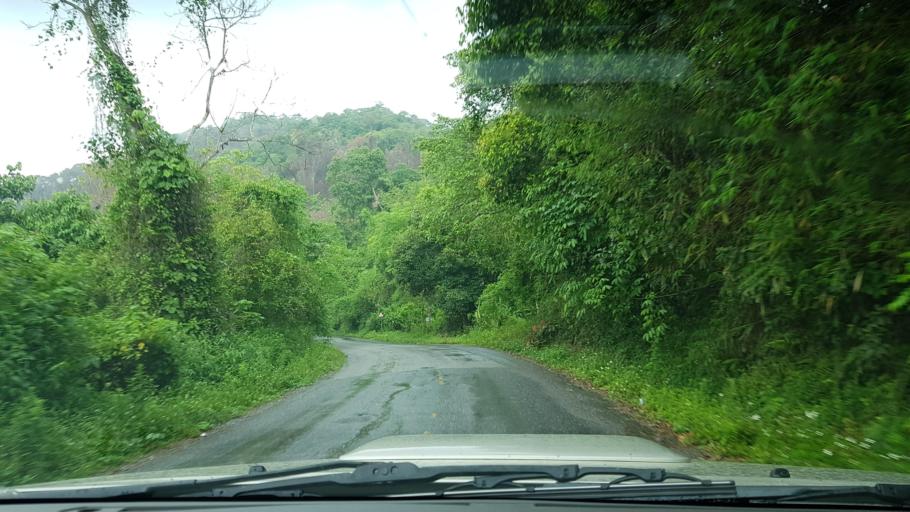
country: LA
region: Oudomxai
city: Muang Xay
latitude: 20.6063
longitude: 101.9453
